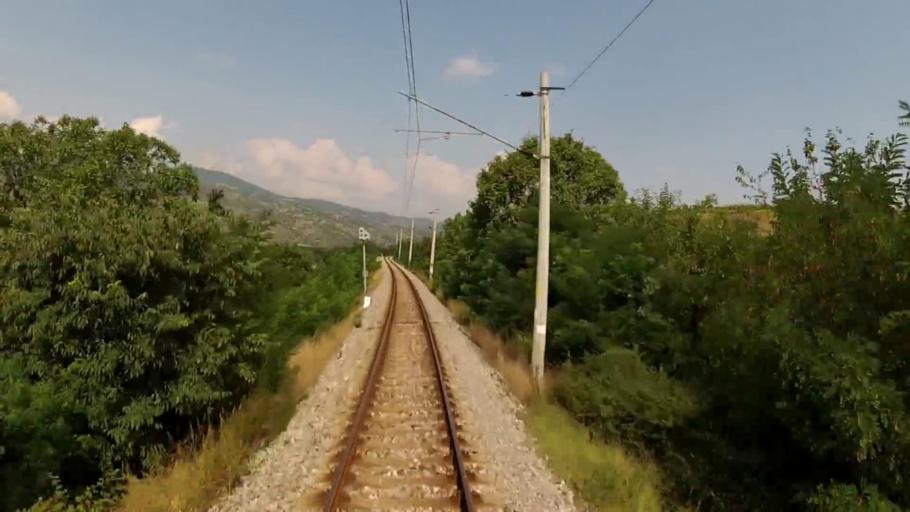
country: BG
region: Blagoevgrad
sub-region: Obshtina Sandanski
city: Sandanski
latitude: 41.5650
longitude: 23.2421
